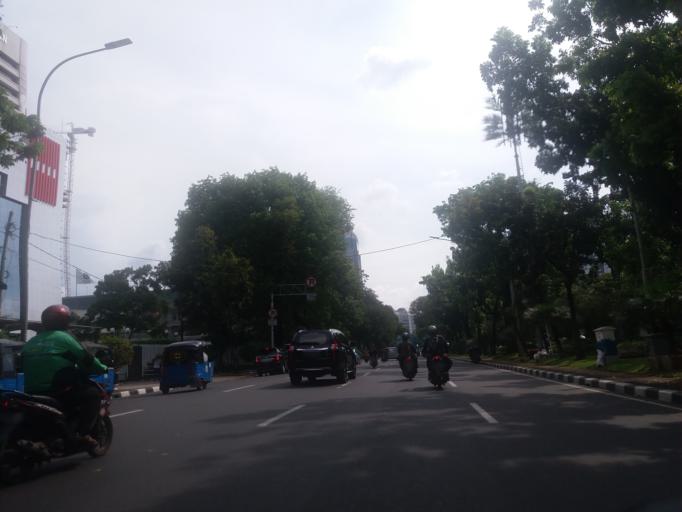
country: ID
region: Jakarta Raya
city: Jakarta
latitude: -6.1806
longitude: 106.8265
